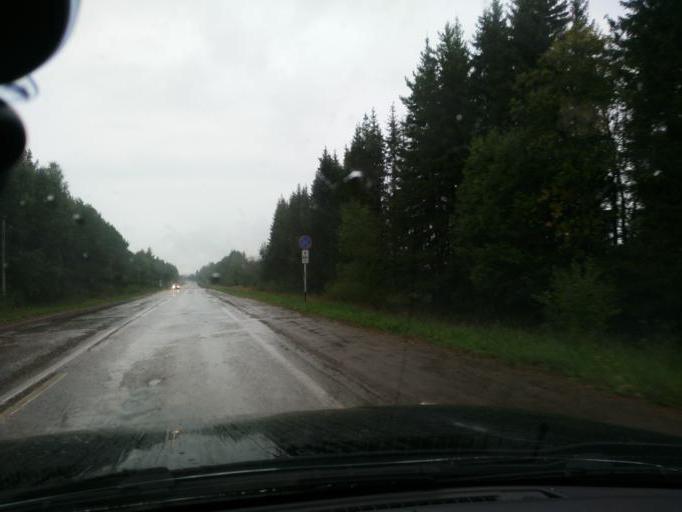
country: RU
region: Perm
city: Osa
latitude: 57.3176
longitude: 55.6218
